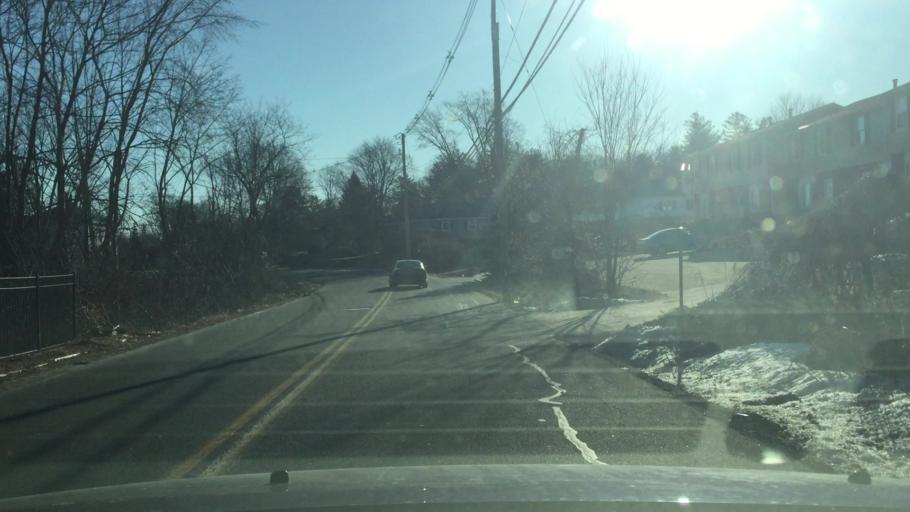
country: US
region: Massachusetts
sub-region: Middlesex County
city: Lowell
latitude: 42.6663
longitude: -71.3475
